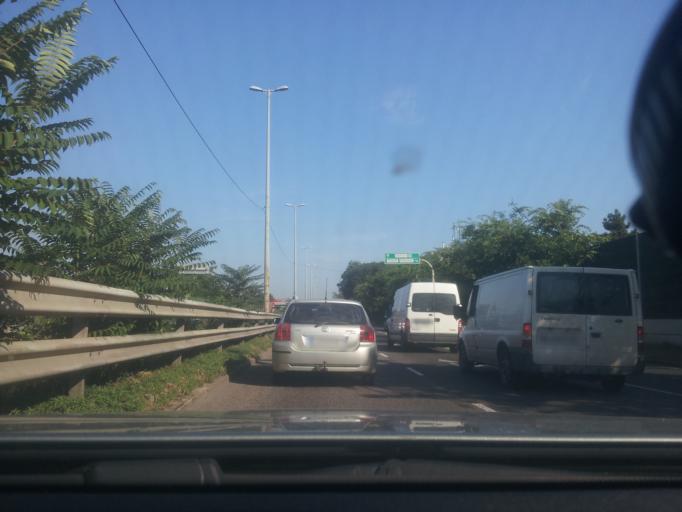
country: HU
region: Budapest
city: Budapest XIX. keruelet
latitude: 47.4463
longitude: 19.1267
